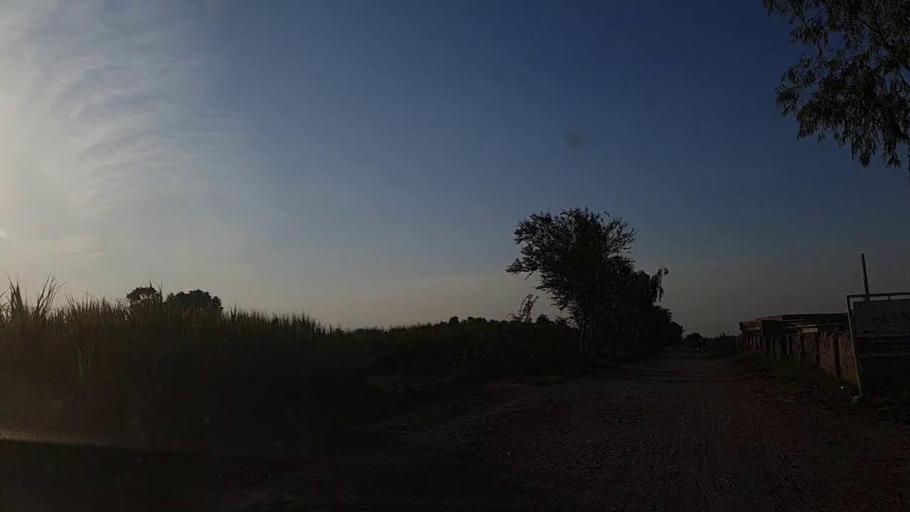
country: PK
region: Sindh
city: Mirpur Batoro
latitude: 24.6818
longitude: 68.2138
